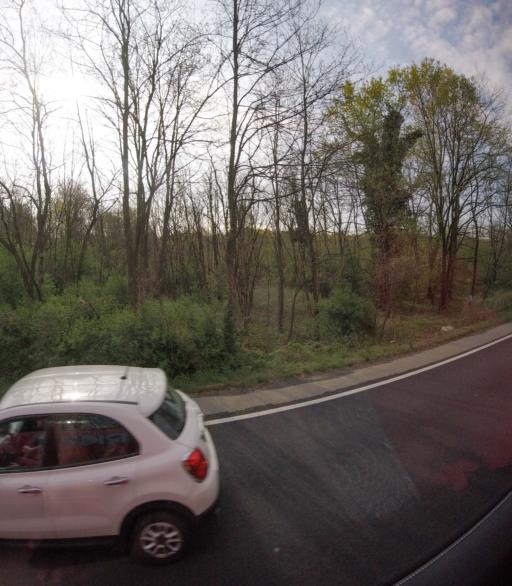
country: IT
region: Piedmont
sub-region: Provincia di Novara
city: Paruzzaro
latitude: 45.7307
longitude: 8.4995
